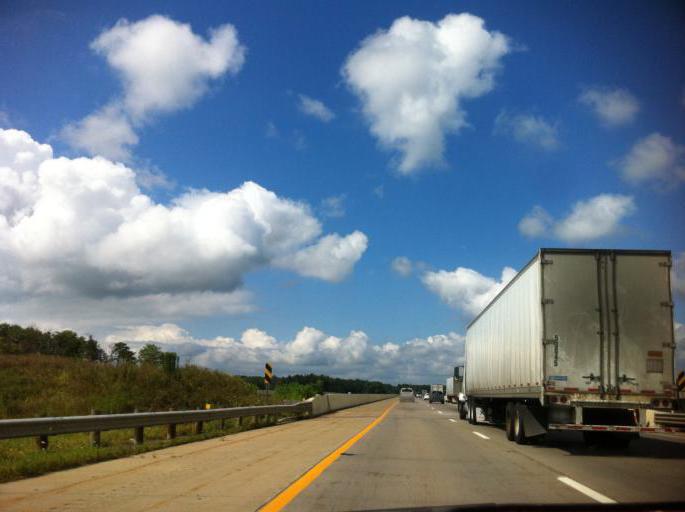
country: US
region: Ohio
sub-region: Mahoning County
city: Austintown
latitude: 41.1158
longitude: -80.8054
